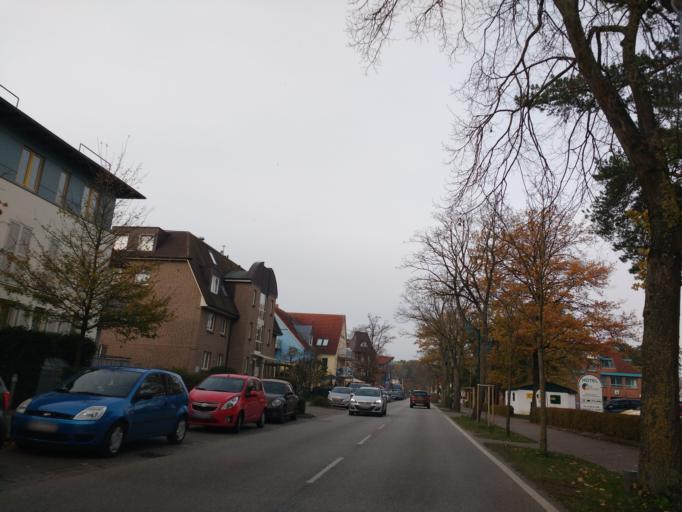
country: DE
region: Mecklenburg-Vorpommern
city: Ostseebad Boltenhagen
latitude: 53.9860
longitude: 11.2069
